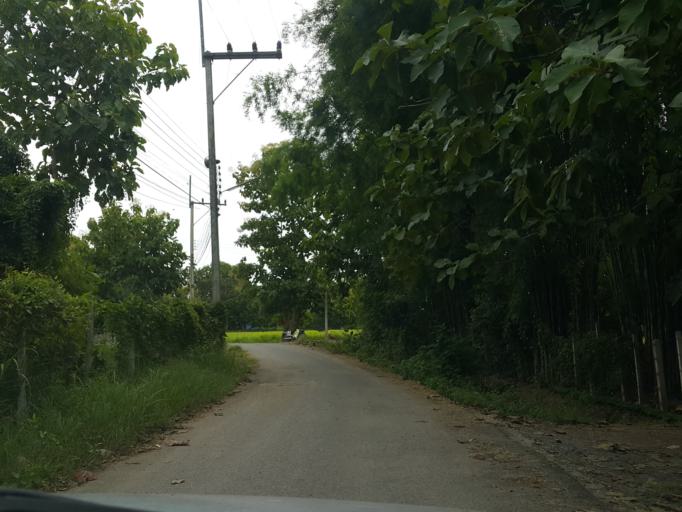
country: TH
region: Chiang Mai
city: San Sai
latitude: 18.8394
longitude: 99.1323
